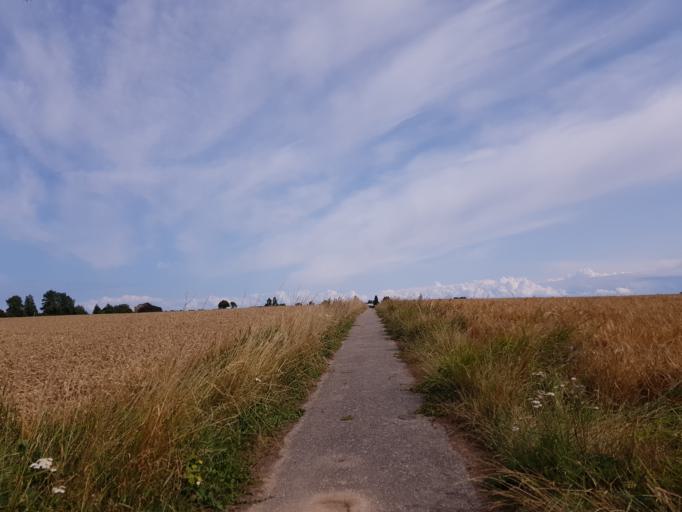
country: DK
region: Zealand
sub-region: Guldborgsund Kommune
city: Nykobing Falster
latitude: 54.5886
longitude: 11.9343
